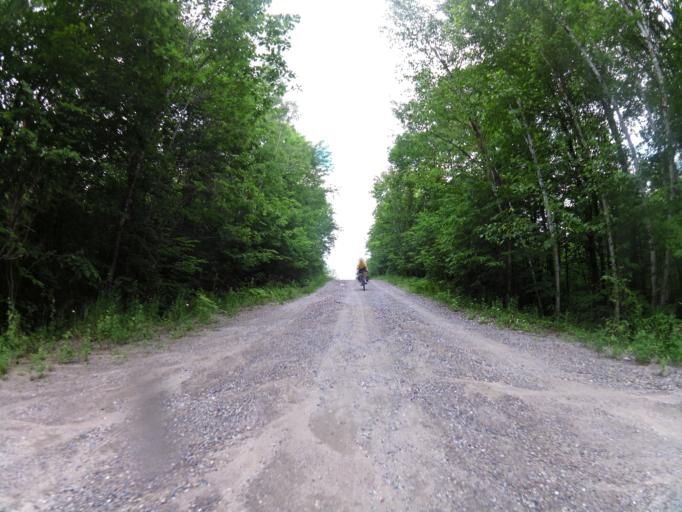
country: CA
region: Ontario
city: Perth
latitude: 45.0251
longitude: -76.5734
